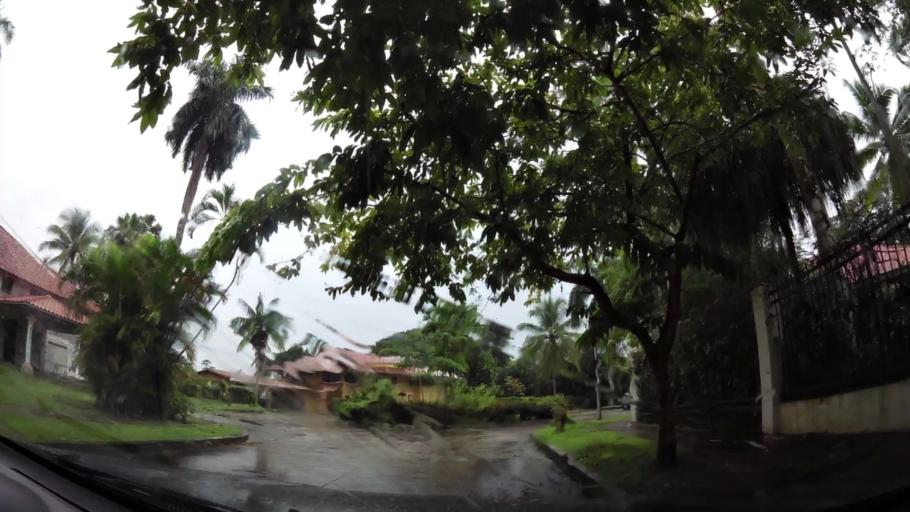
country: PA
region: Panama
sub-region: Distrito de Panama
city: Ancon
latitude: 8.9788
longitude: -79.5575
